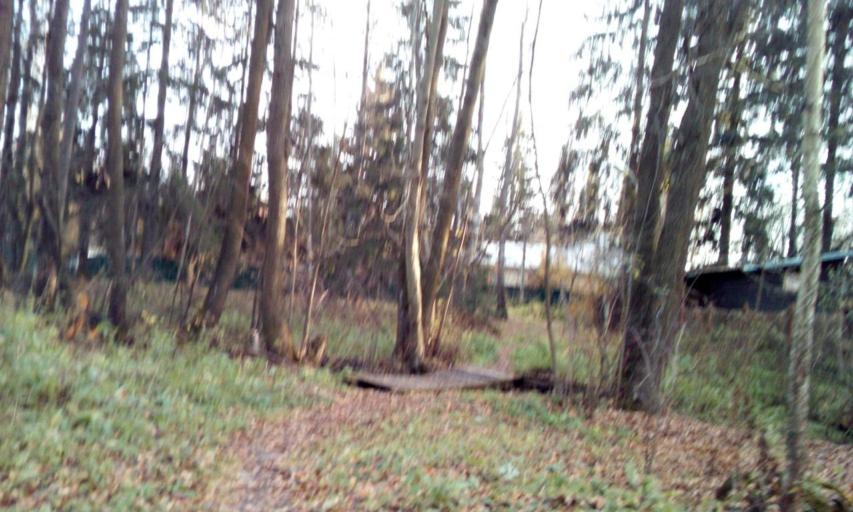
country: RU
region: Moskovskaya
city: Aprelevka
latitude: 55.5682
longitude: 37.1013
